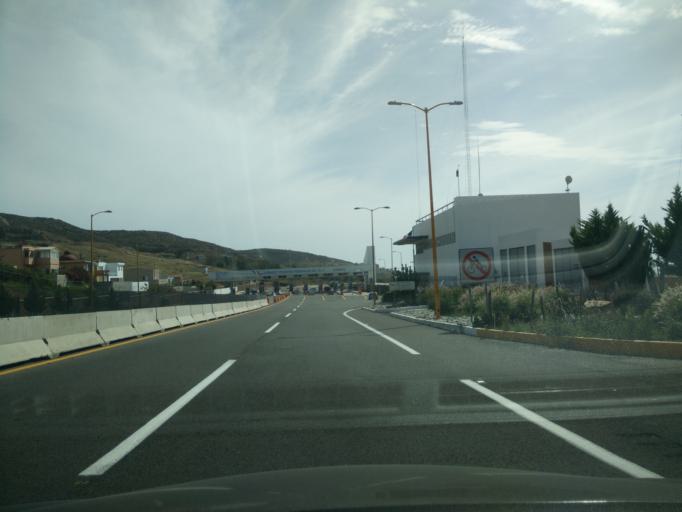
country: MX
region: Baja California
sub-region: Tijuana
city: La Esperanza [Granjas Familiares]
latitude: 32.5158
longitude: -117.1090
